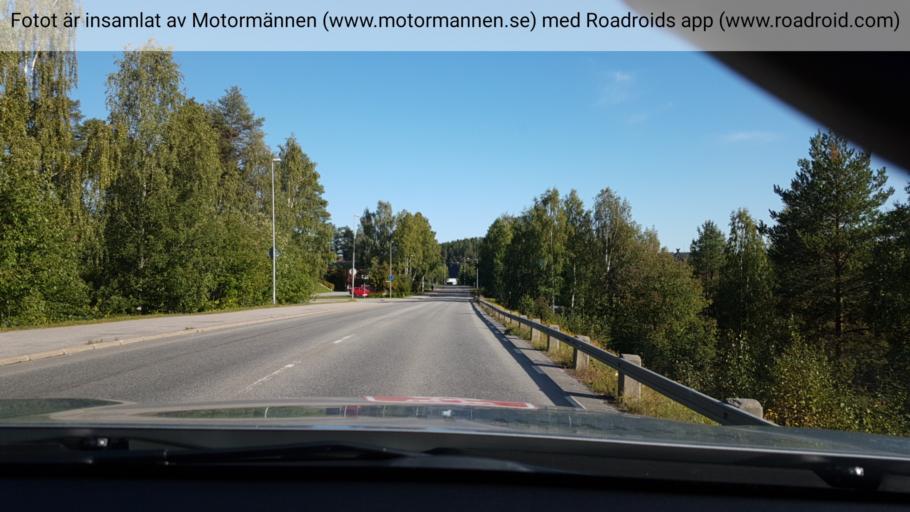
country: SE
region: Vaesterbotten
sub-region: Lycksele Kommun
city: Lycksele
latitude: 64.5866
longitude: 18.6822
